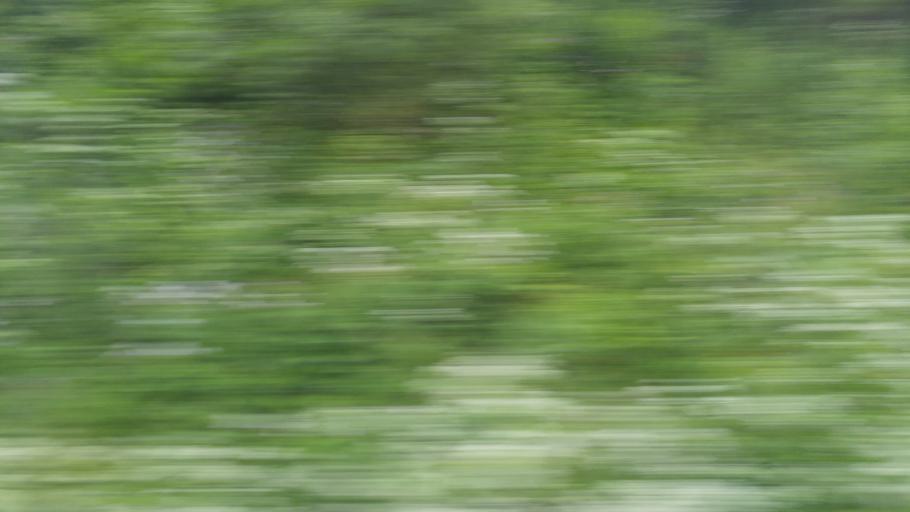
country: NO
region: Nord-Trondelag
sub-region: Levanger
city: Levanger
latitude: 63.4564
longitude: 11.4150
